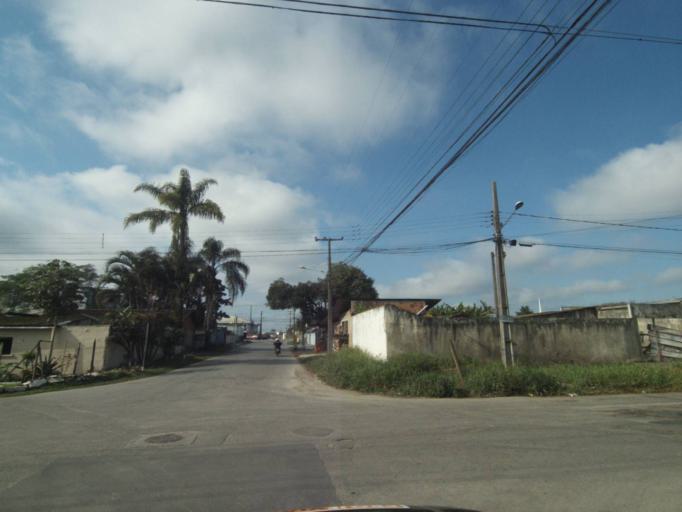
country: BR
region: Parana
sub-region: Paranagua
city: Paranagua
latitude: -25.5560
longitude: -48.5572
